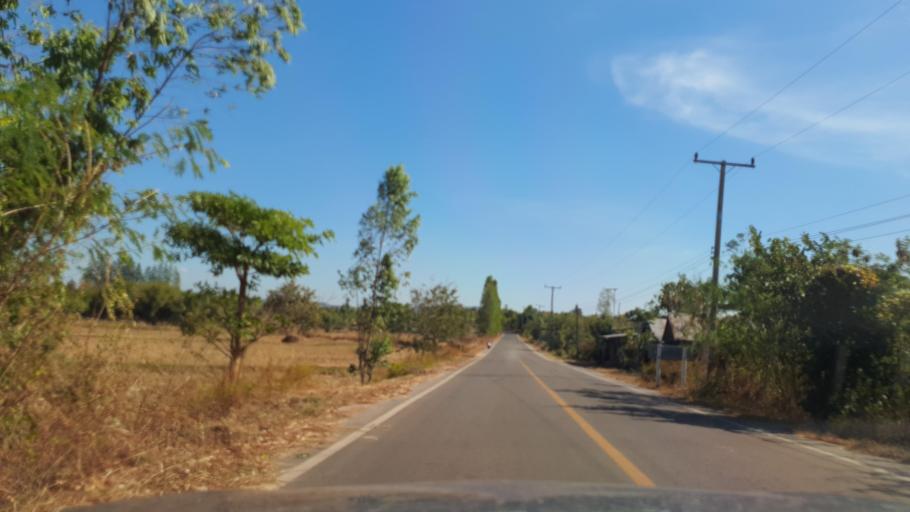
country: TH
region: Kalasin
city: Khao Wong
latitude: 16.6890
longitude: 104.1145
